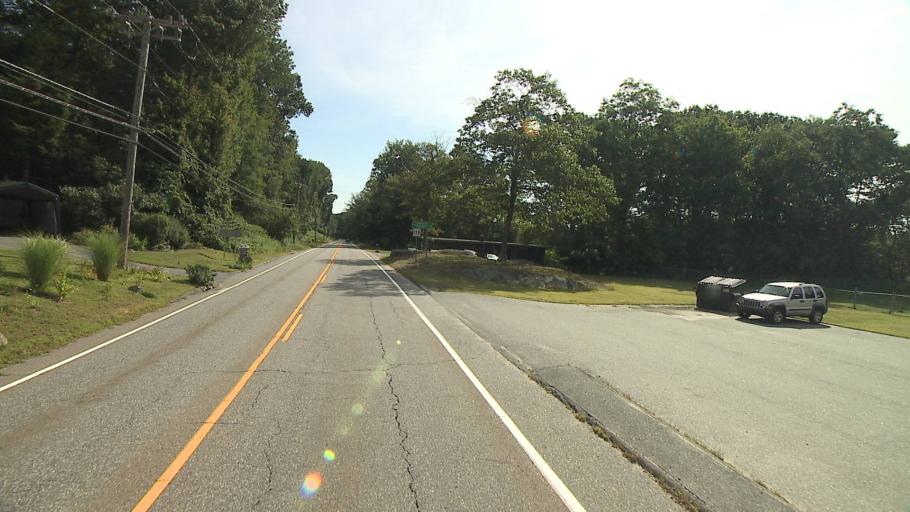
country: US
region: Connecticut
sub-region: Litchfield County
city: Northwest Harwinton
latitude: 41.7673
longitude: -73.0847
